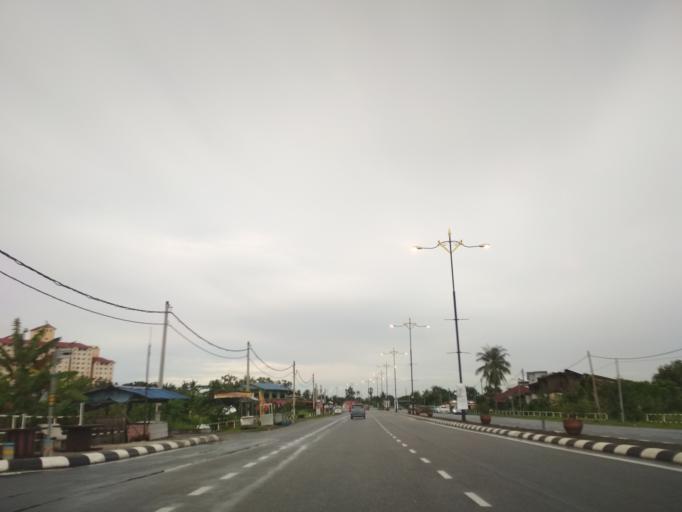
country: MY
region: Perlis
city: Kangar
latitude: 6.4332
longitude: 100.1976
